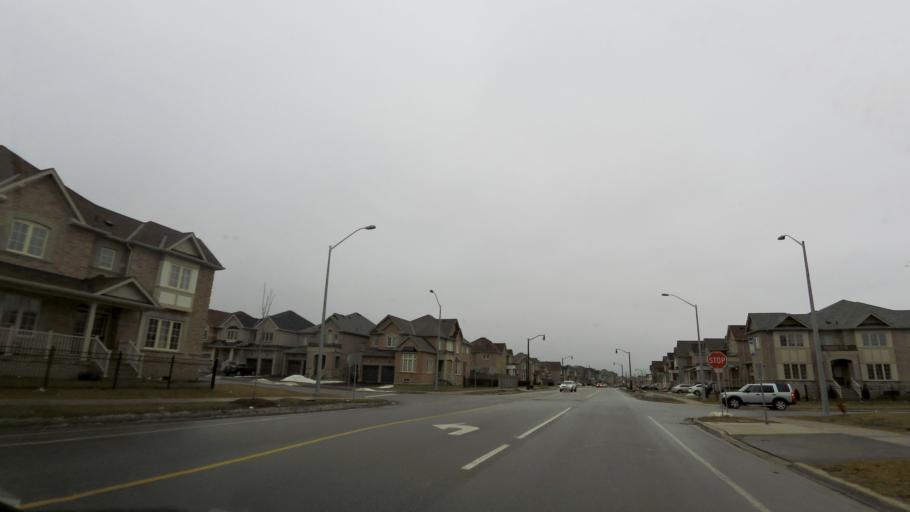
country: CA
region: Ontario
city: Brampton
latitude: 43.7940
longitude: -79.6733
